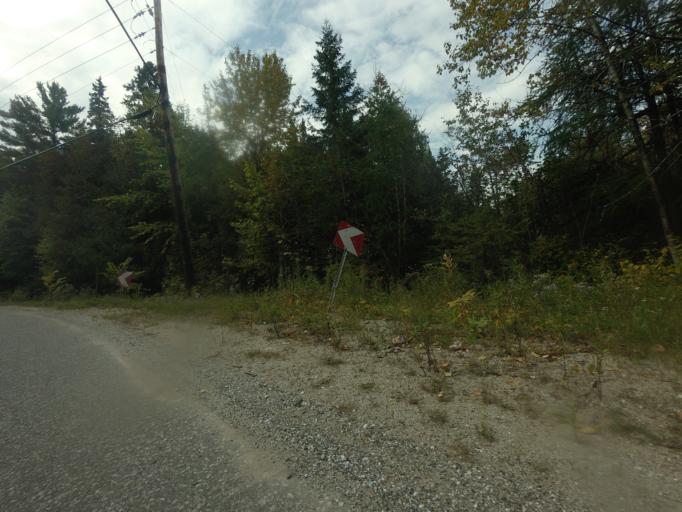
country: CA
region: Quebec
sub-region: Outaouais
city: Wakefield
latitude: 45.9710
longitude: -75.9368
